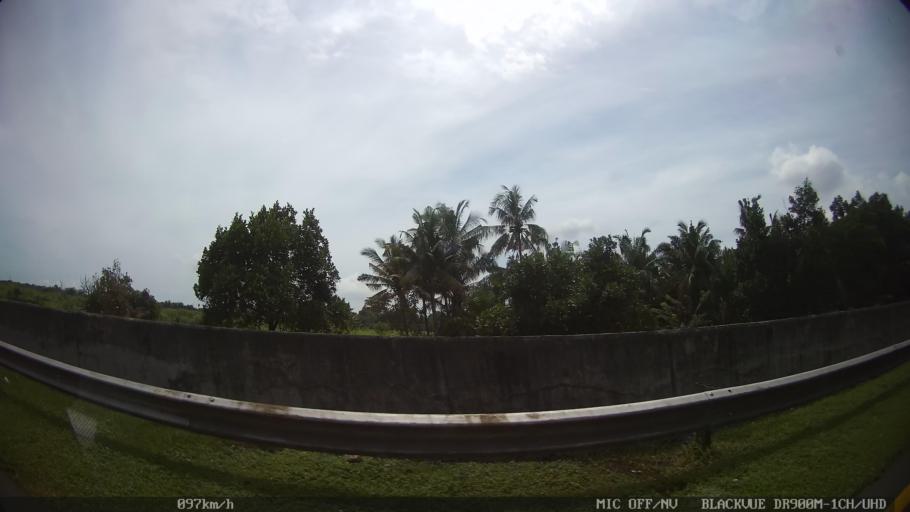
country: ID
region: North Sumatra
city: Labuhan Deli
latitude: 3.7102
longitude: 98.6820
